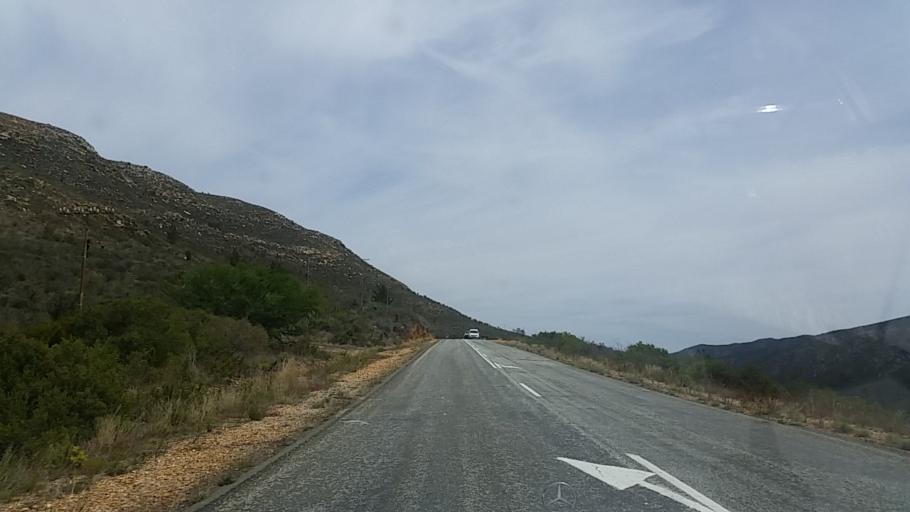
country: ZA
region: Western Cape
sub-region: Eden District Municipality
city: Knysna
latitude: -33.7456
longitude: 22.9882
